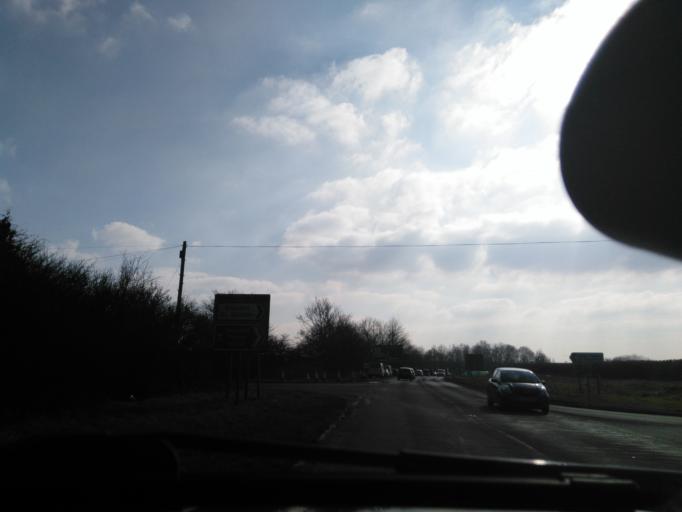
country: GB
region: England
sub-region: Wiltshire
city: Chippenham
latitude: 51.5184
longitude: -2.1203
